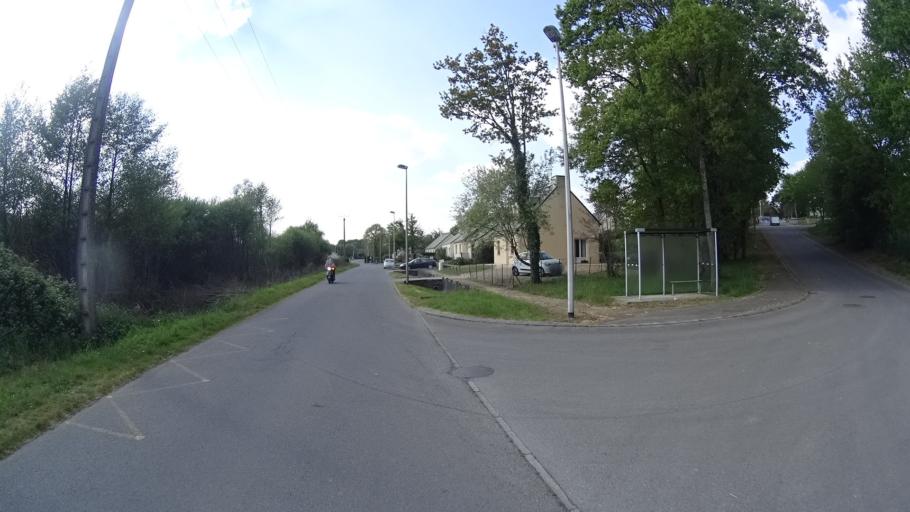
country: FR
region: Pays de la Loire
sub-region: Departement de la Loire-Atlantique
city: Saint-Nicolas-de-Redon
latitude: 47.6384
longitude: -2.0678
